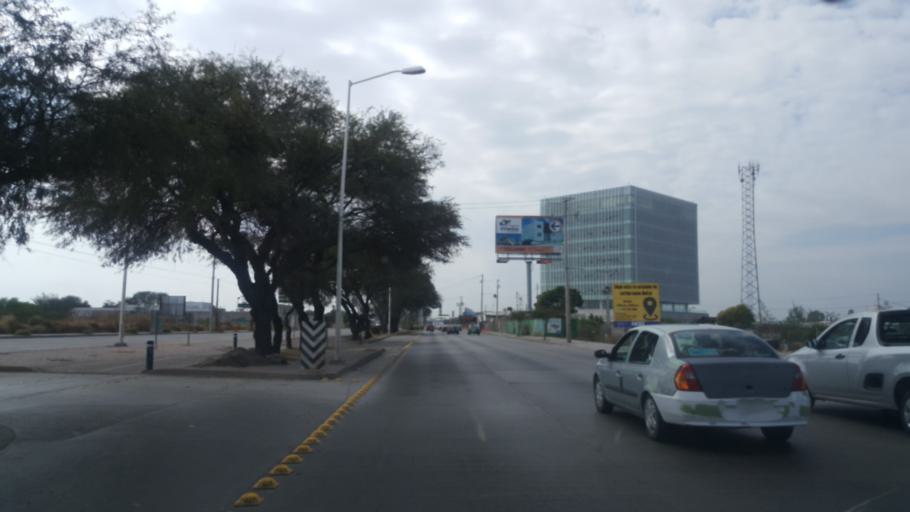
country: MX
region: Guanajuato
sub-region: Leon
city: Fraccionamiento Paraiso Real
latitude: 21.0974
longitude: -101.6155
